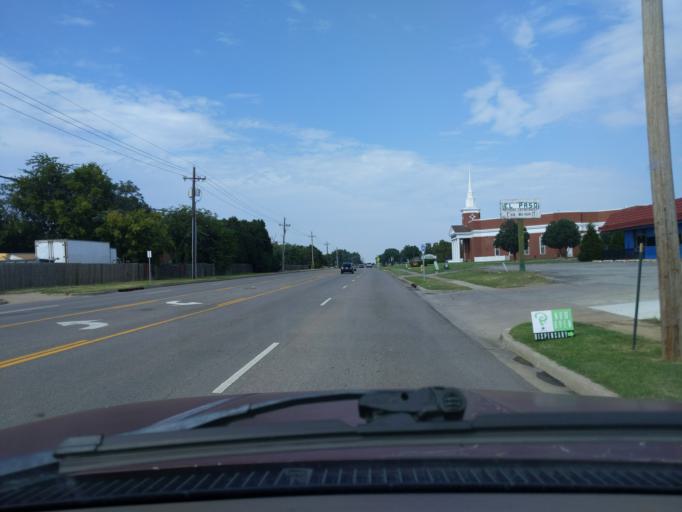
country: US
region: Oklahoma
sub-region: Tulsa County
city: Broken Arrow
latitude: 36.1348
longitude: -95.8331
